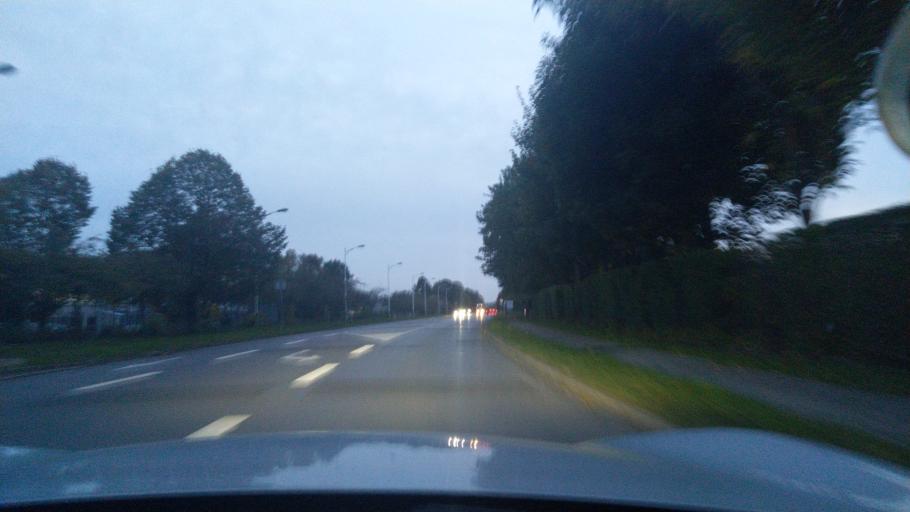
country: FR
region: Ile-de-France
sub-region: Departement de Seine-et-Marne
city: Lognes
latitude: 48.8215
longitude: 2.6361
